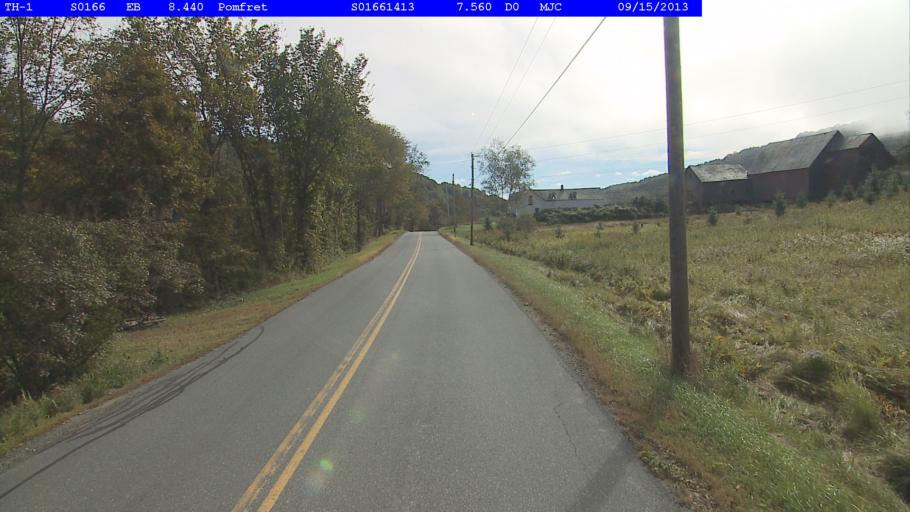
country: US
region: Vermont
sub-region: Windsor County
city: Woodstock
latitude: 43.7256
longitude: -72.4720
